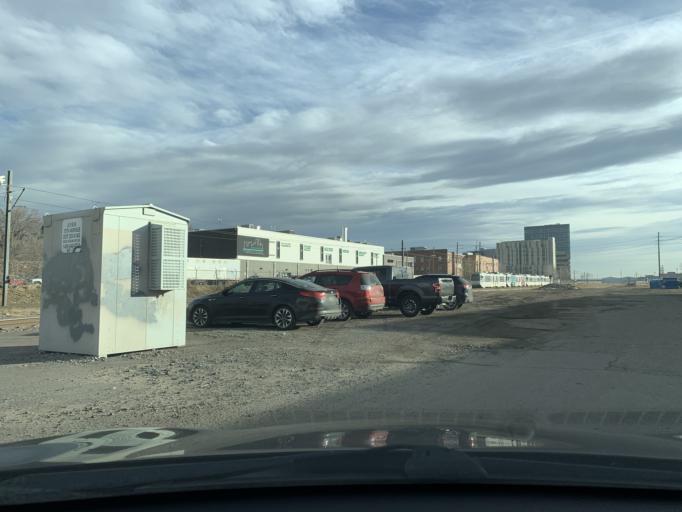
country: US
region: Colorado
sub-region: Denver County
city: Denver
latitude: 39.7368
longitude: -105.0066
